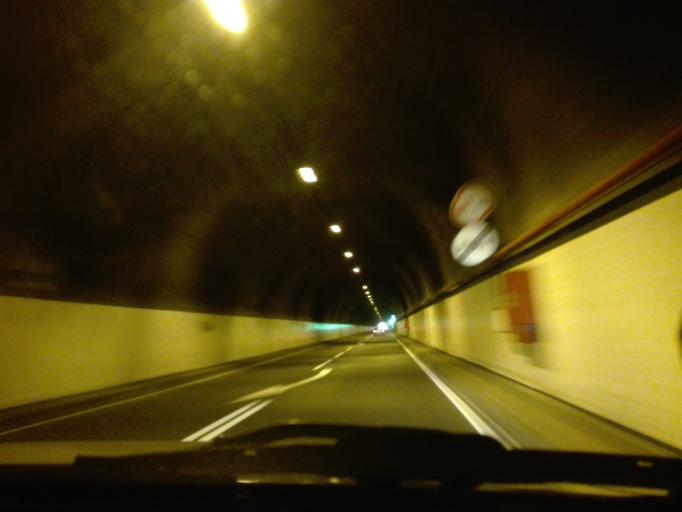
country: PT
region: Madeira
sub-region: Machico
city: Machico
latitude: 32.7339
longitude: -16.7933
